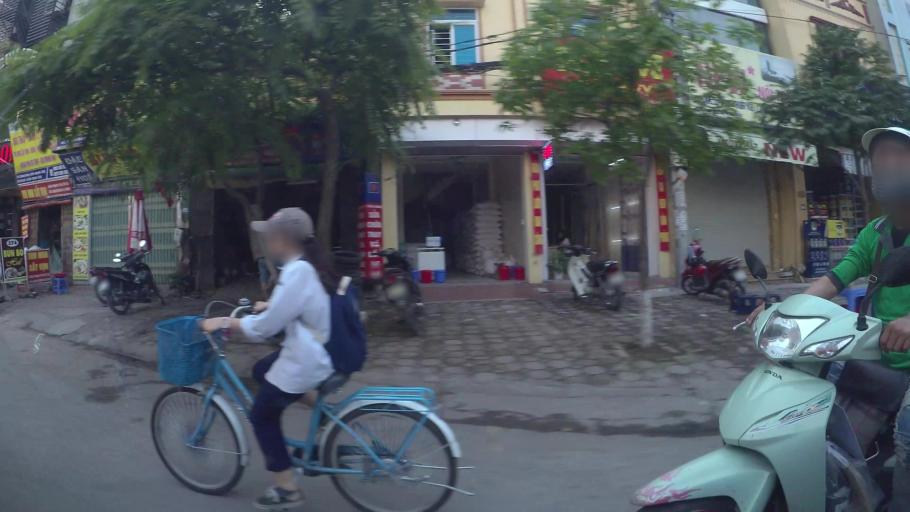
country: VN
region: Ha Noi
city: Thanh Xuan
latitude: 20.9751
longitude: 105.8248
